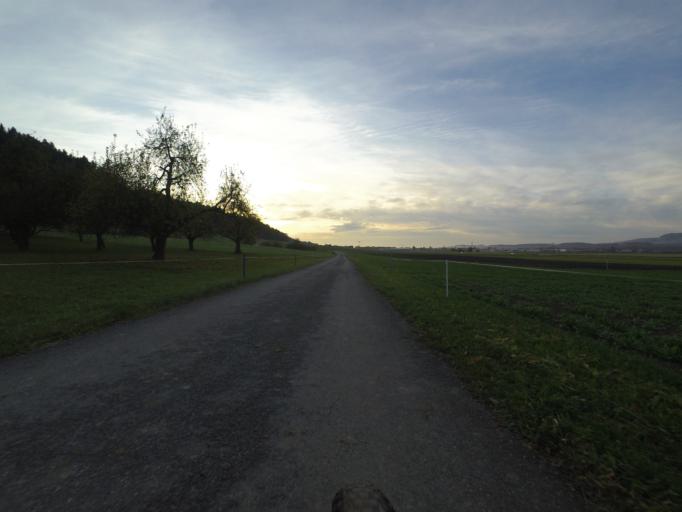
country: CH
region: Thurgau
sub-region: Frauenfeld District
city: Pfyn
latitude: 47.5758
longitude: 8.9645
